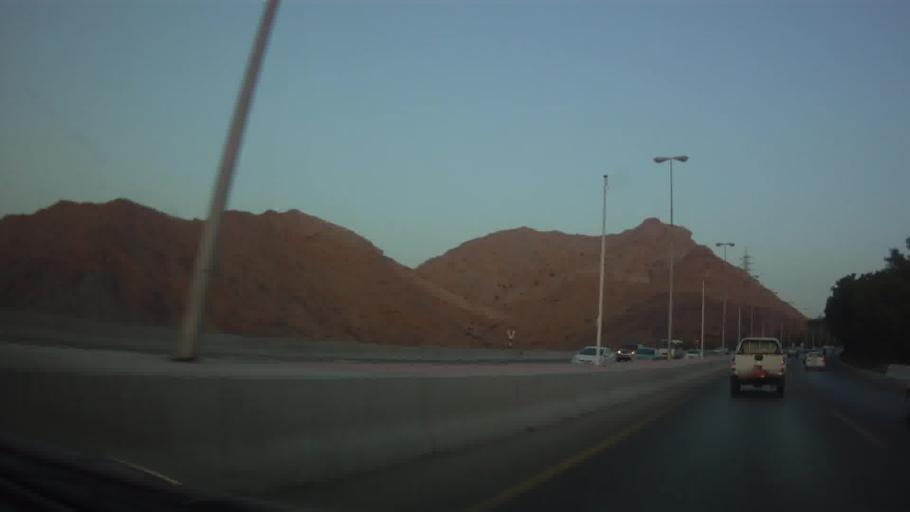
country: OM
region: Muhafazat Masqat
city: Muscat
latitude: 23.6180
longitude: 58.5216
